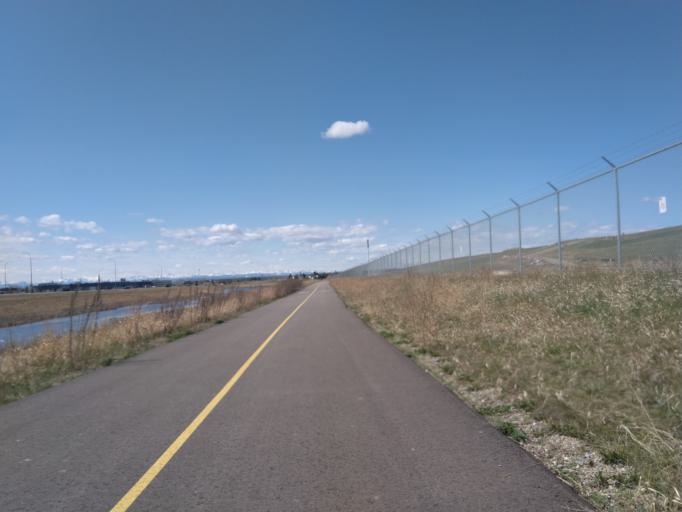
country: CA
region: Alberta
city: Chestermere
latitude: 51.0160
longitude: -113.9489
